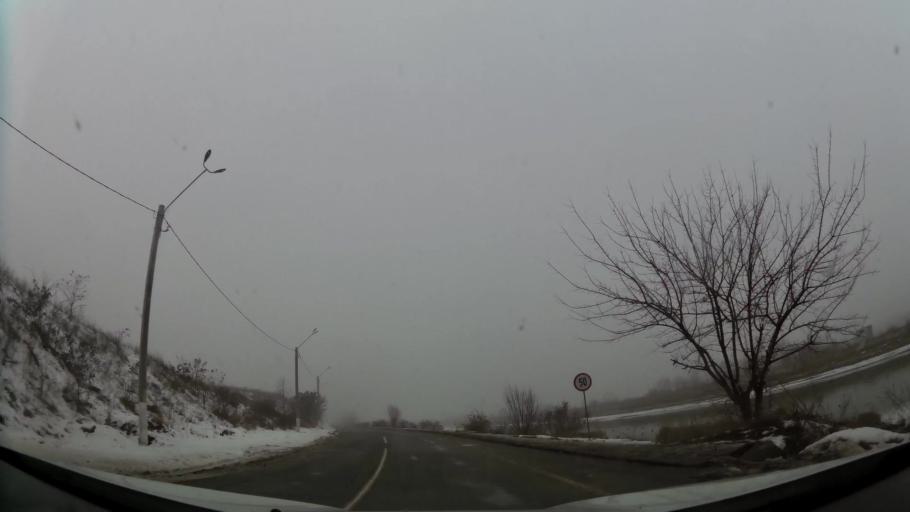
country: RO
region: Ilfov
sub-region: Comuna Chiajna
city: Chiajna
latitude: 44.4629
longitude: 25.9922
